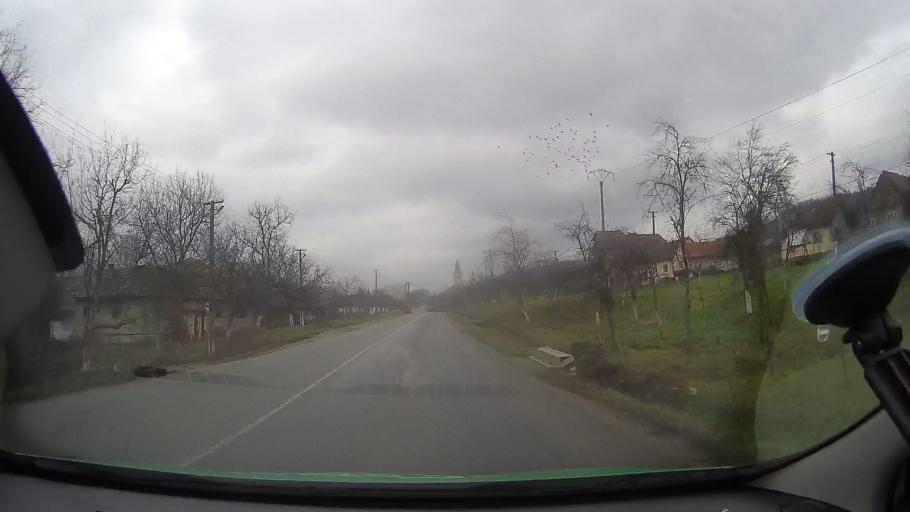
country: RO
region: Arad
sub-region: Comuna Buteni
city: Buteni
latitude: 46.2998
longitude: 22.1749
